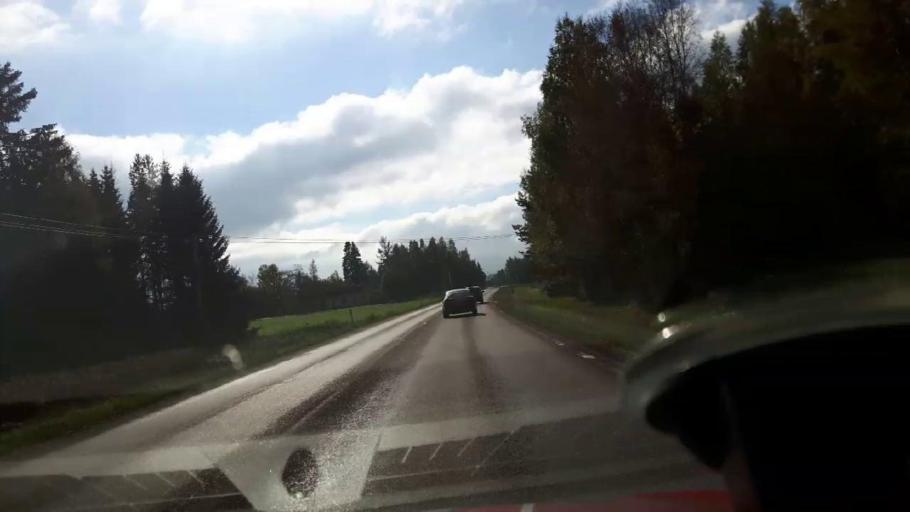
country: SE
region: Gaevleborg
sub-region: Bollnas Kommun
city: Arbra
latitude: 61.5241
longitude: 16.3640
